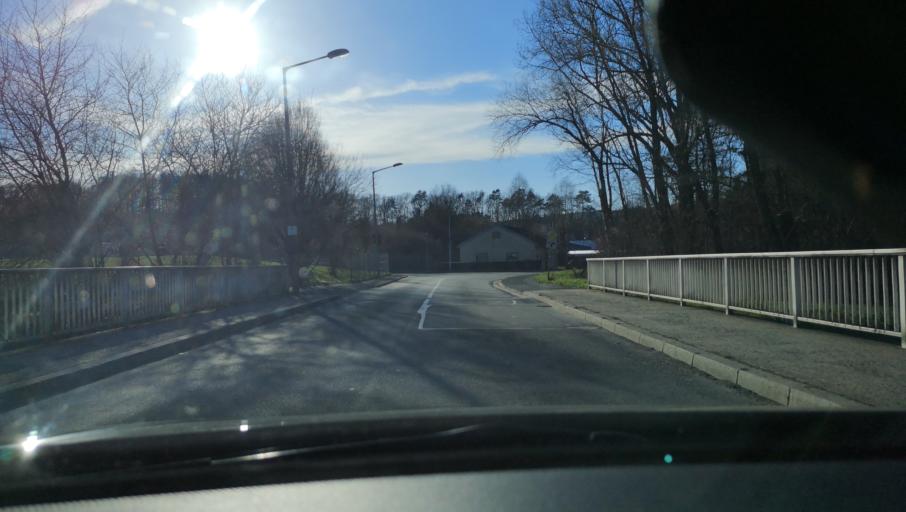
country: DE
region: Bavaria
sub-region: Upper Franconia
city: Neustadt bei Coburg
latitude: 50.3215
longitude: 11.1112
